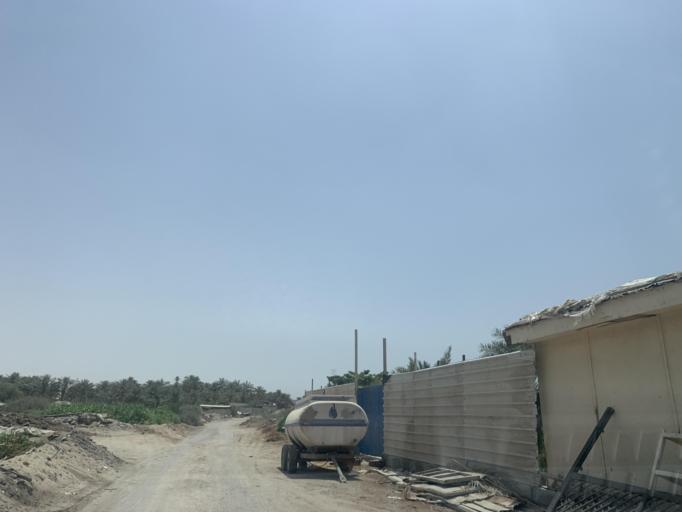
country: BH
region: Central Governorate
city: Madinat Hamad
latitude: 26.1553
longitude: 50.4986
